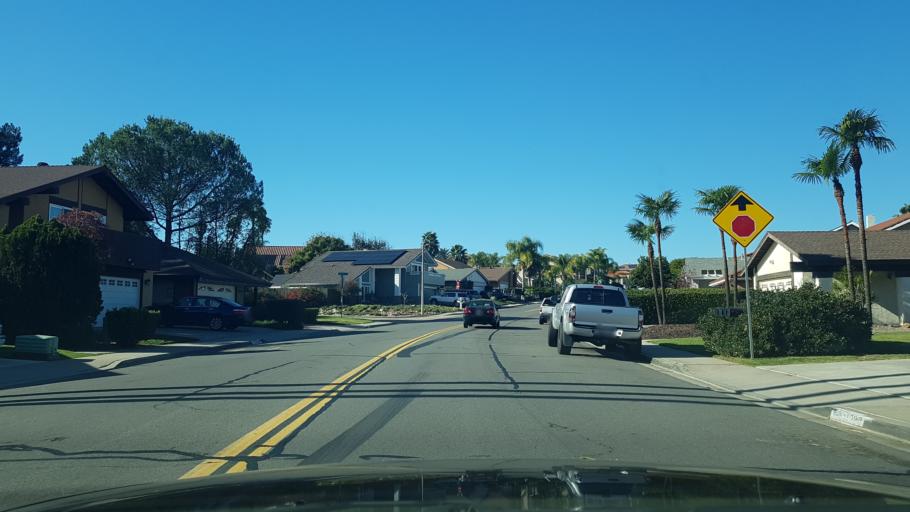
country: US
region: California
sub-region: San Diego County
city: Poway
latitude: 33.0338
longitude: -117.0811
